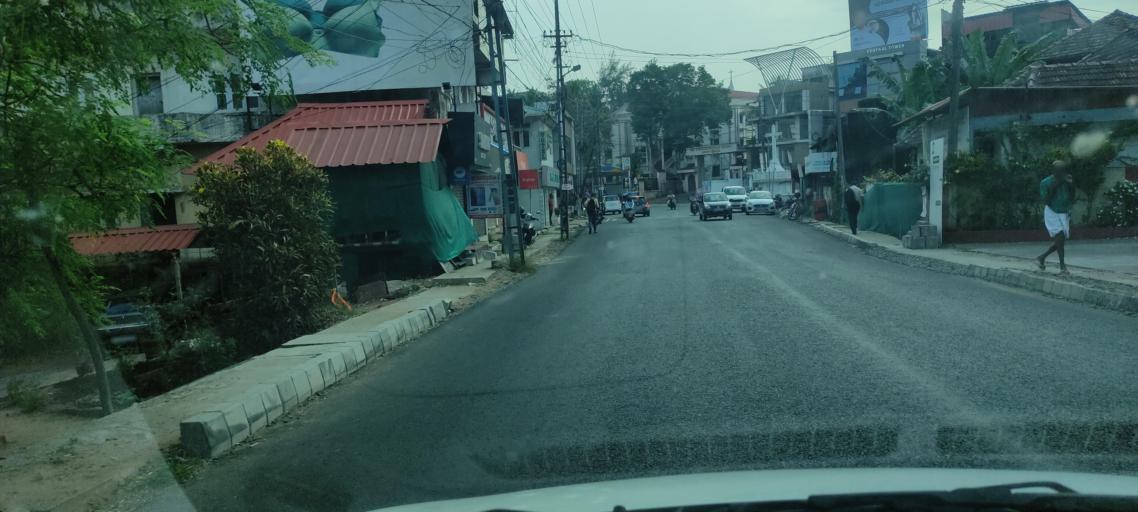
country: IN
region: Kerala
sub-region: Pattanamtitta
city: Tiruvalla
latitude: 9.3827
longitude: 76.5734
